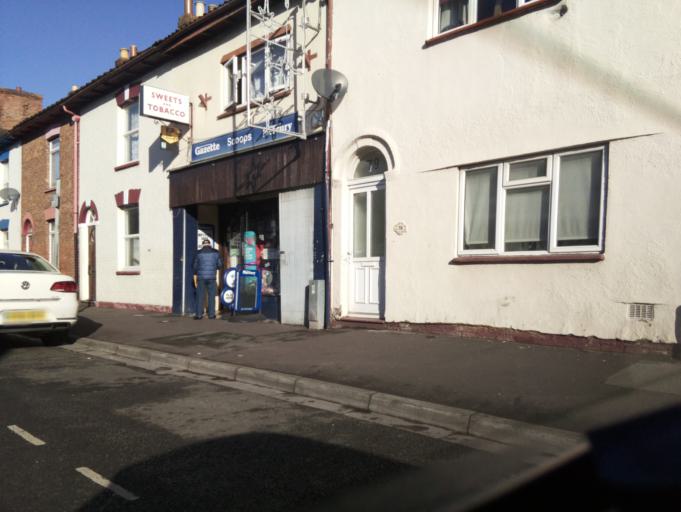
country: GB
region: England
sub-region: Somerset
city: Bridgwater
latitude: 51.1281
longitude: -2.9944
